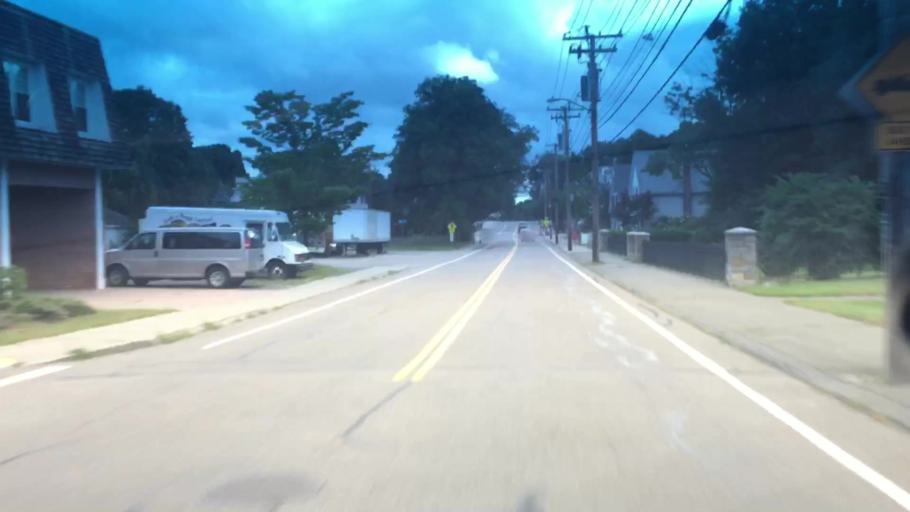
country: US
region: Massachusetts
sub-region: Norfolk County
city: Walpole
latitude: 42.1573
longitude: -71.2172
